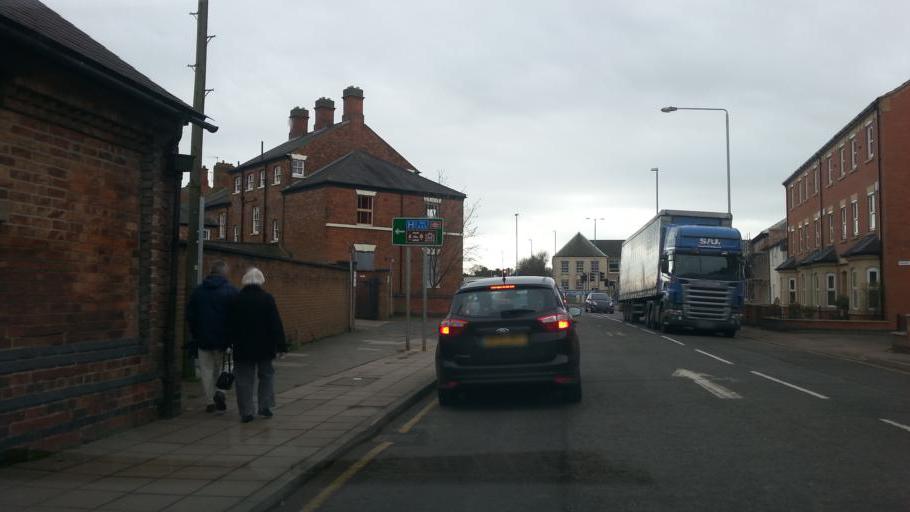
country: GB
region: England
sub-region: Leicestershire
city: Melton Mowbray
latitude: 52.7677
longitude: -0.8905
